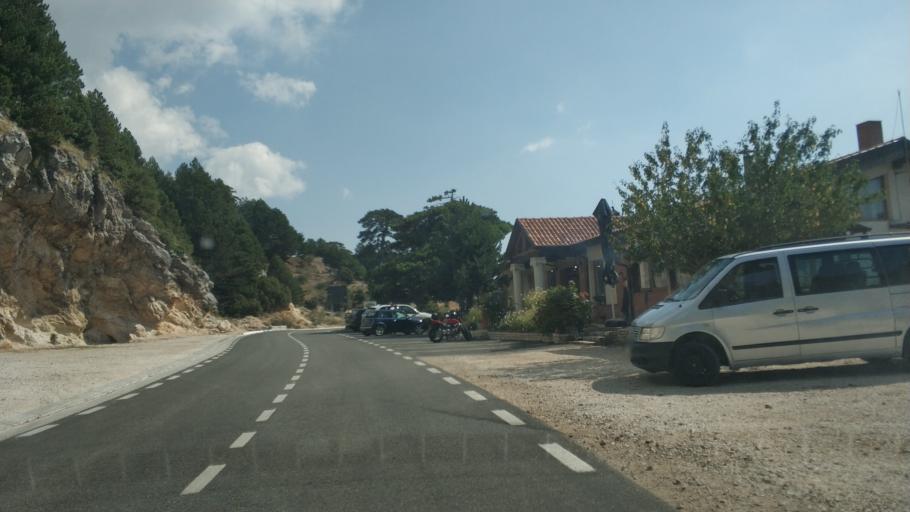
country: AL
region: Vlore
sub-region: Rrethi i Vlores
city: Vranisht
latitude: 40.1967
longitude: 19.5979
